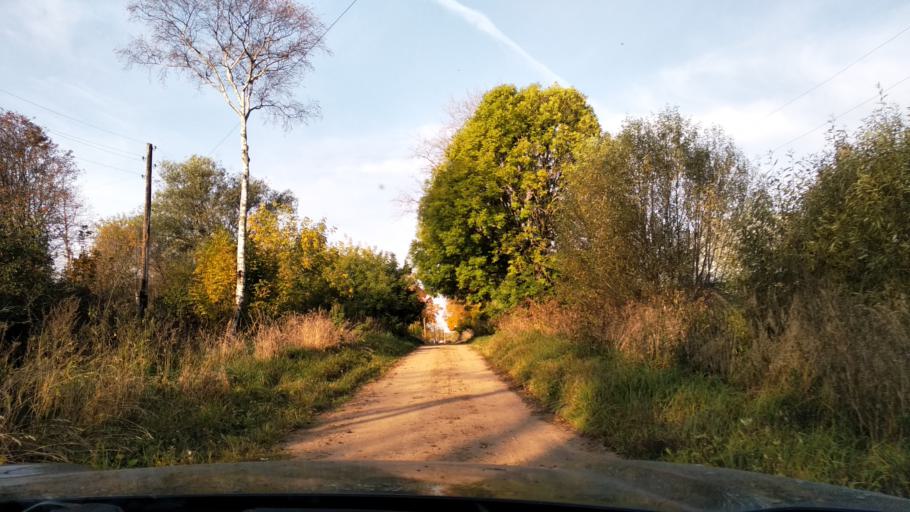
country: RU
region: Tverskaya
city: Krasnyy Kholm
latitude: 58.0095
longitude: 37.1900
